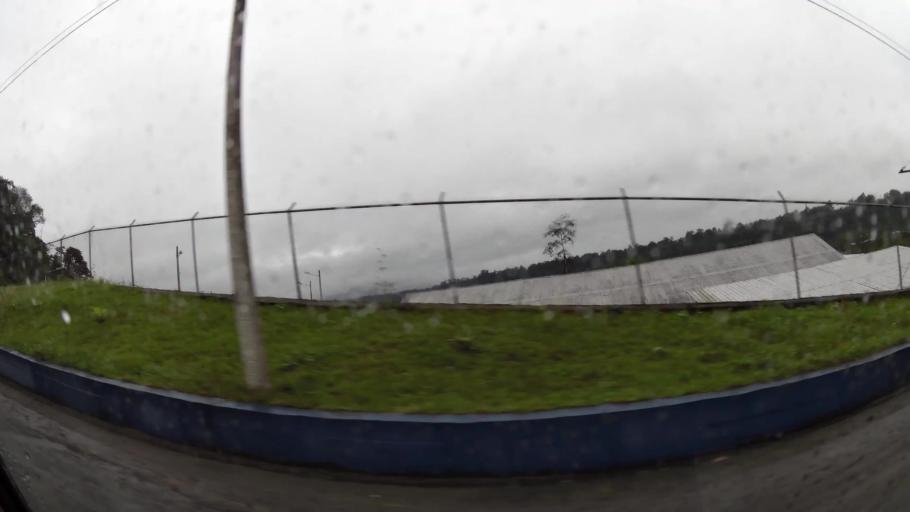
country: EC
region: Santo Domingo de los Tsachilas
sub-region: Canton Santo Domingo de los Colorados
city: Santo Domingo de los Colorados
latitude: -0.2494
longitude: -79.1400
